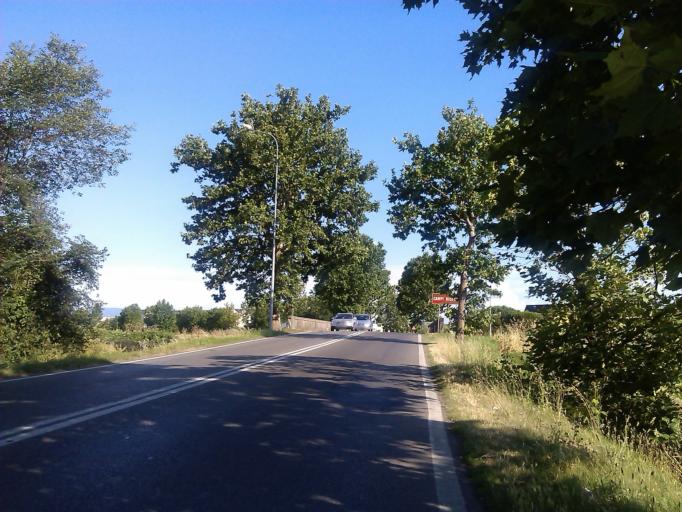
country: IT
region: Tuscany
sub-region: Province of Florence
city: San Donnino
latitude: 43.8137
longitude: 11.1557
